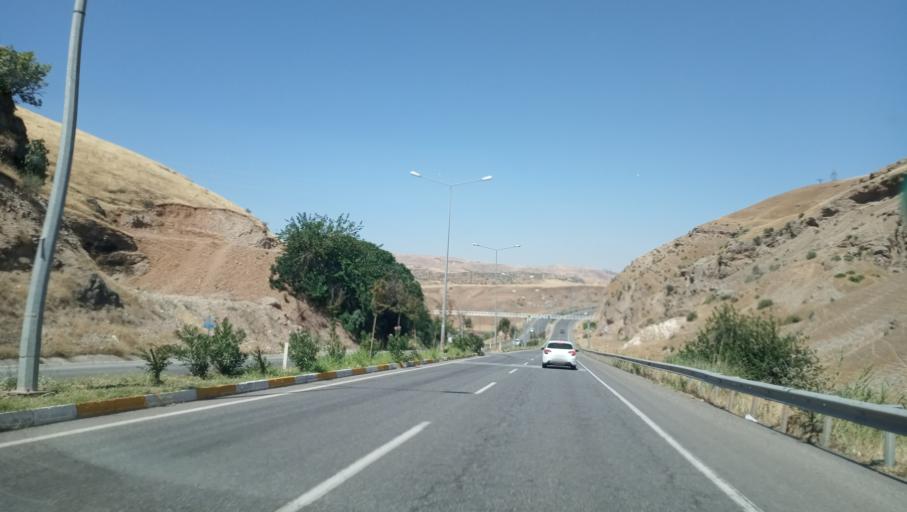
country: TR
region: Siirt
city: Civankan
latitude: 37.9491
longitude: 41.8682
